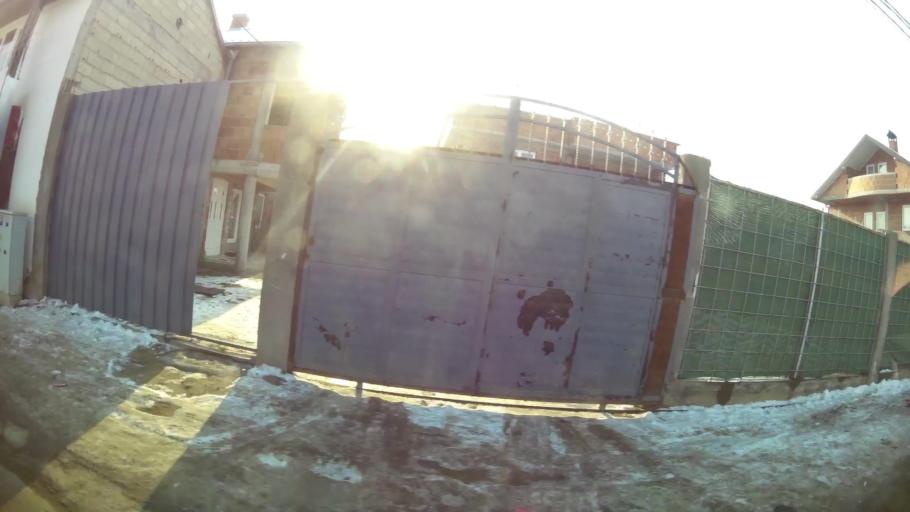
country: MK
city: Creshevo
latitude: 42.0217
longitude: 21.5014
